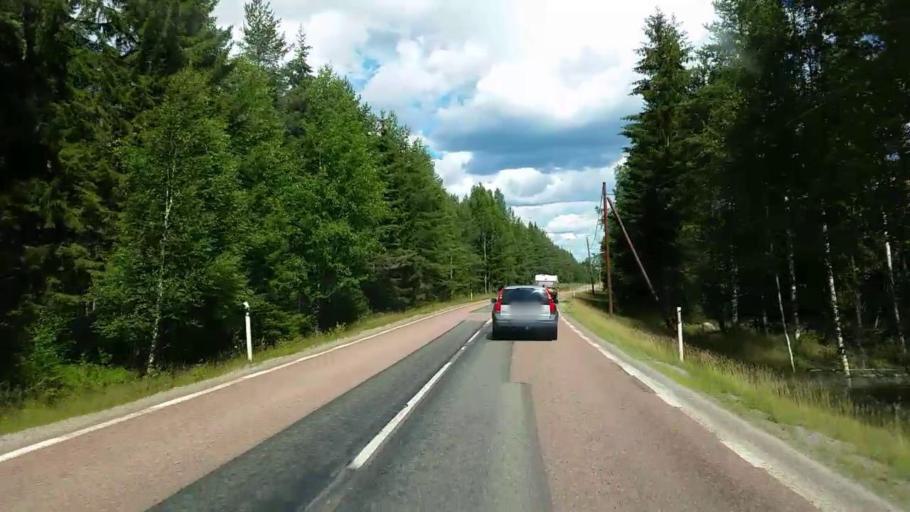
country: SE
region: Gaevleborg
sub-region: Ovanakers Kommun
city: Edsbyn
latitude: 61.3495
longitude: 15.6779
